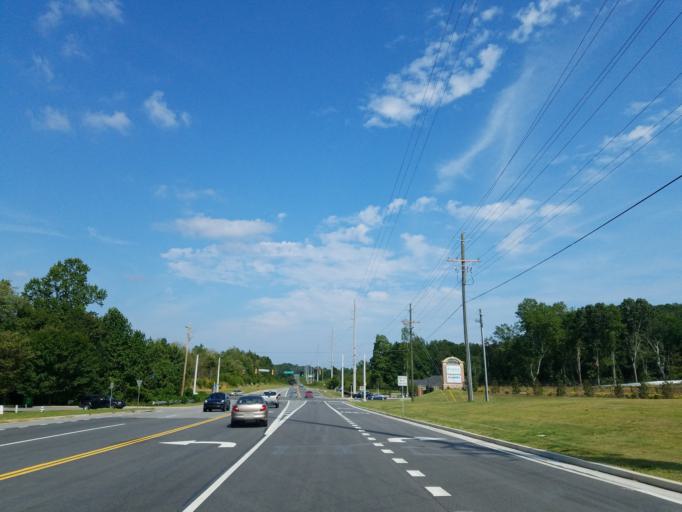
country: US
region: Georgia
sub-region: Dawson County
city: Dawsonville
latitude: 34.3534
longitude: -84.0454
